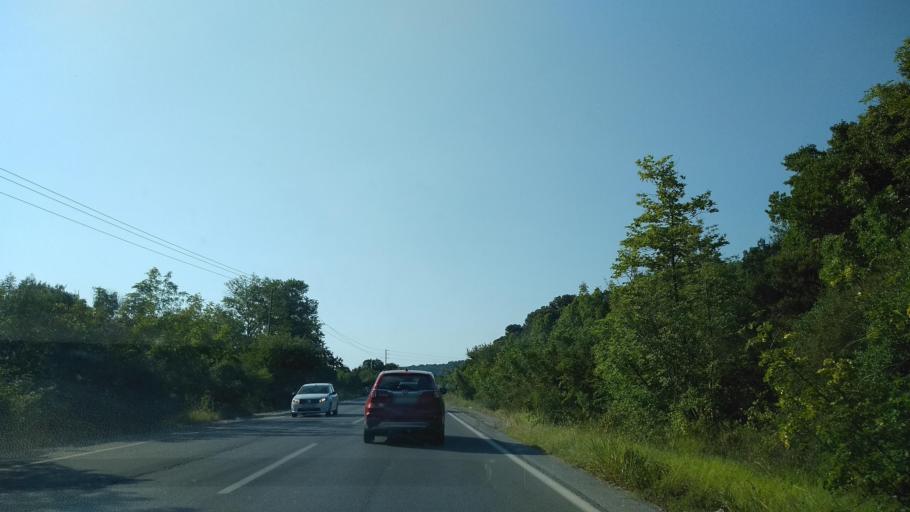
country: GR
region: Central Macedonia
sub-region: Nomos Thessalonikis
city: Stavros
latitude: 40.6451
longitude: 23.7460
